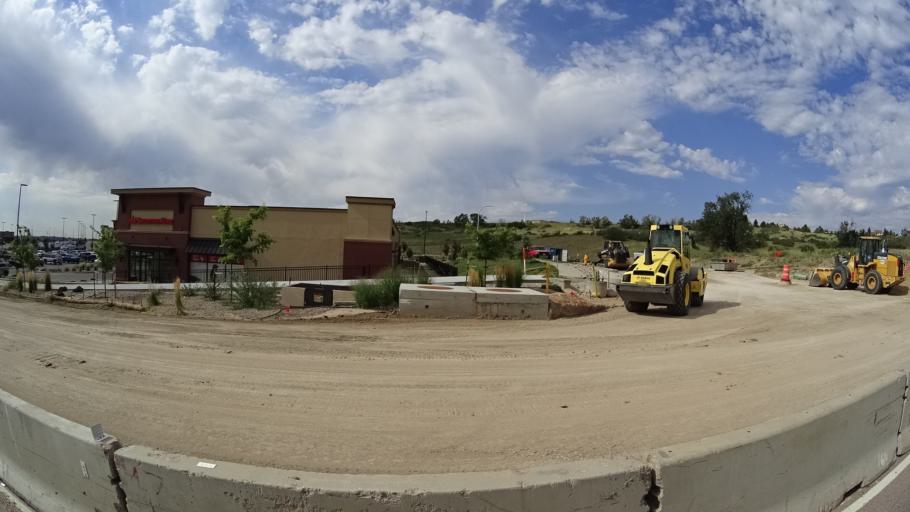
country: US
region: Colorado
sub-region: El Paso County
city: Cimarron Hills
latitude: 38.8944
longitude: -104.7235
